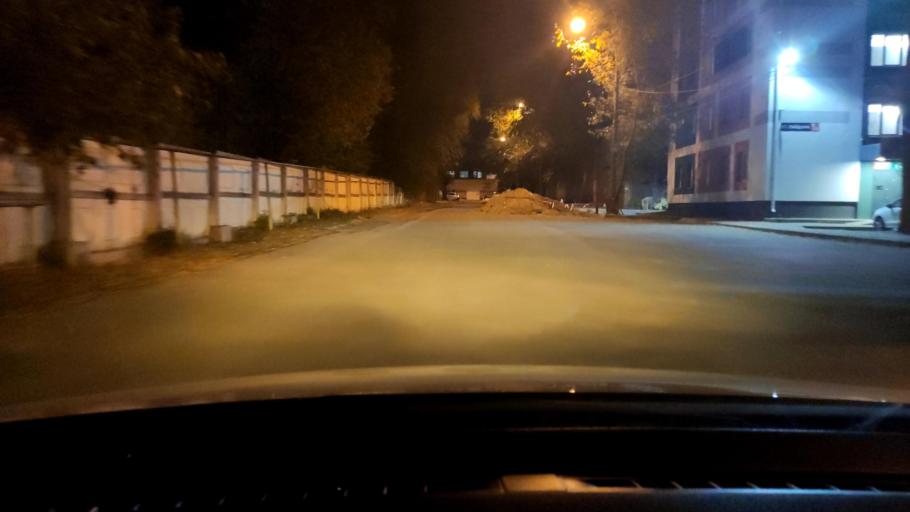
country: RU
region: Voronezj
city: Voronezh
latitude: 51.6783
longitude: 39.1417
